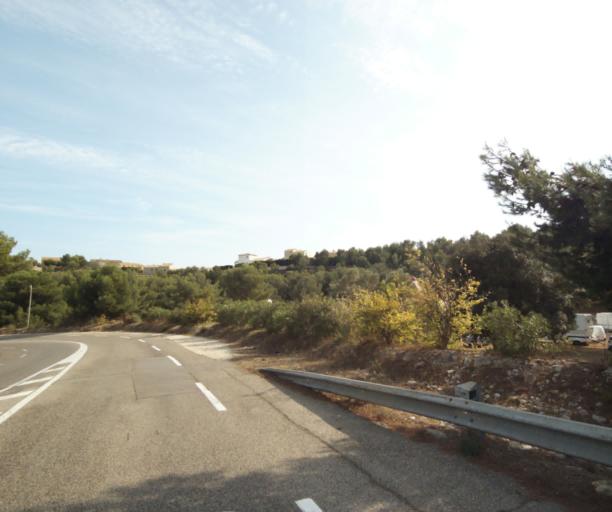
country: FR
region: Provence-Alpes-Cote d'Azur
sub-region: Departement des Bouches-du-Rhone
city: Sausset-les-Pins
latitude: 43.3388
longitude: 5.1046
